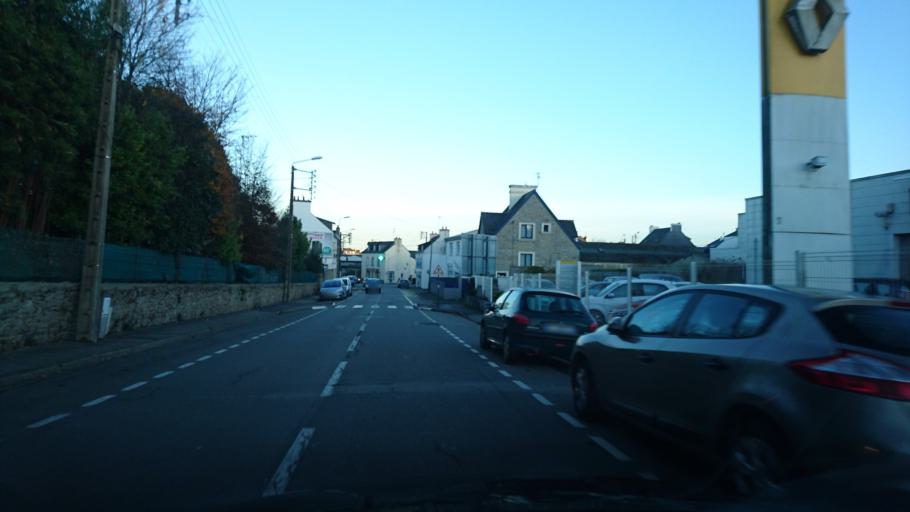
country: FR
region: Brittany
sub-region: Departement du Finistere
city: Quimperle
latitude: 47.8718
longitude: -3.5573
